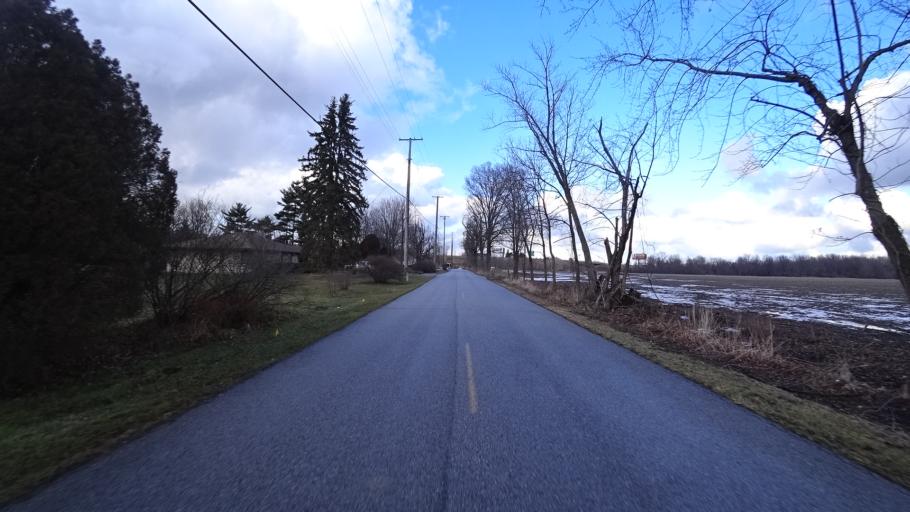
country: US
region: Indiana
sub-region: Porter County
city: Porter
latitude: 41.6110
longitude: -87.0867
